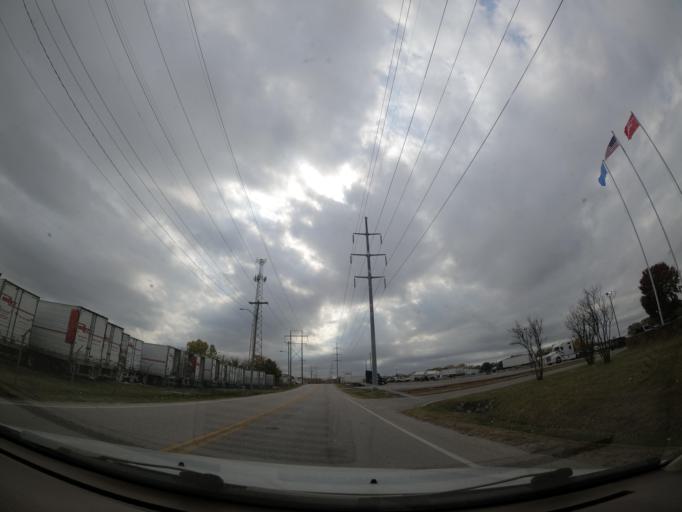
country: US
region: Oklahoma
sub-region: Tulsa County
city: Tulsa
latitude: 36.1017
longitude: -95.9936
